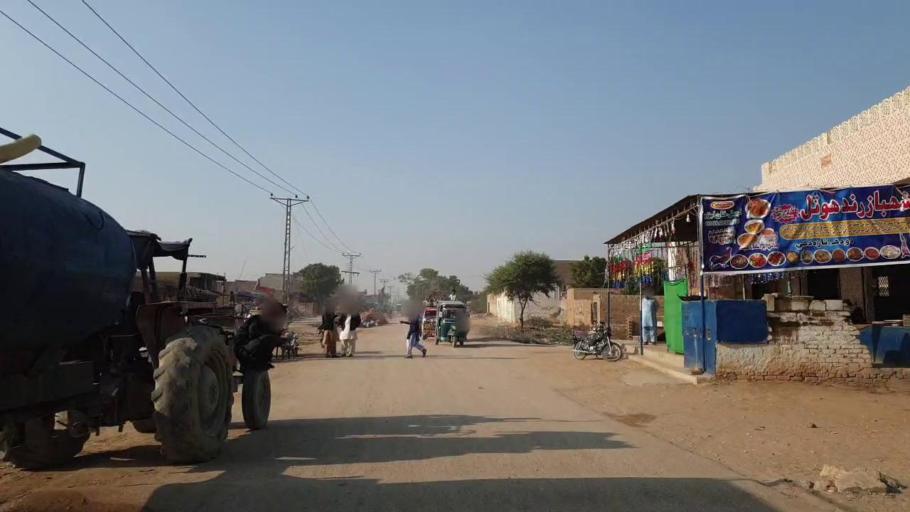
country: PK
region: Sindh
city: Kotri
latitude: 25.3550
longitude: 68.2577
